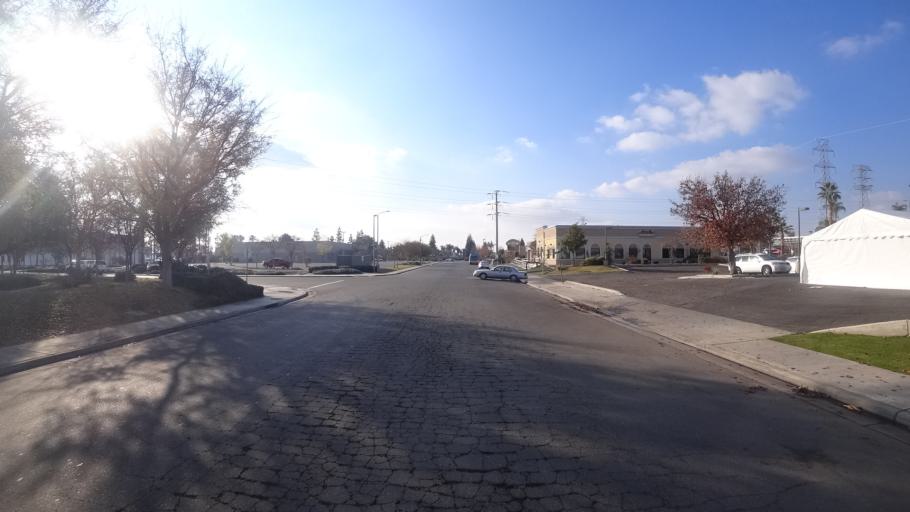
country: US
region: California
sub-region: Kern County
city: Greenacres
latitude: 35.3167
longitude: -119.0899
